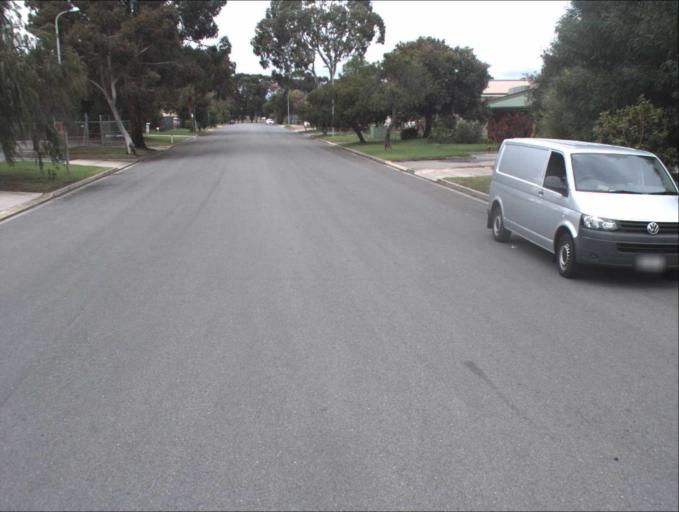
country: AU
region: South Australia
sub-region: Port Adelaide Enfield
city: Blair Athol
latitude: -34.8570
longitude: 138.5702
